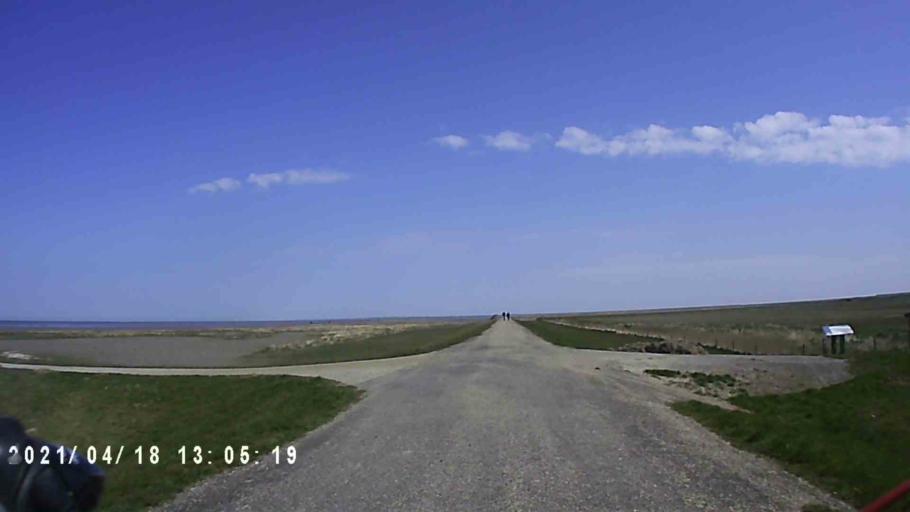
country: NL
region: Friesland
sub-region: Gemeente Dongeradeel
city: Anjum
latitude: 53.4036
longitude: 6.0869
